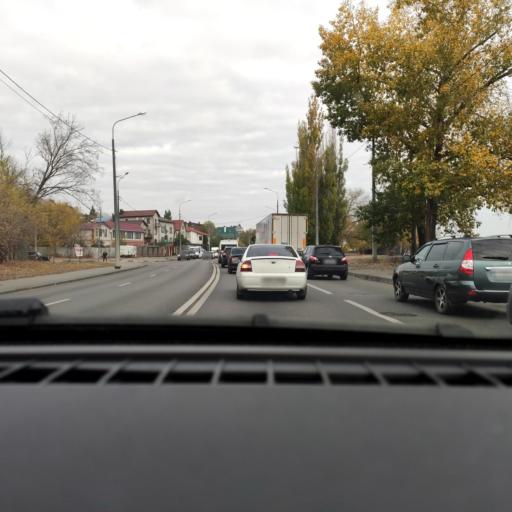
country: RU
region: Voronezj
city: Voronezh
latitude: 51.6779
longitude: 39.2271
